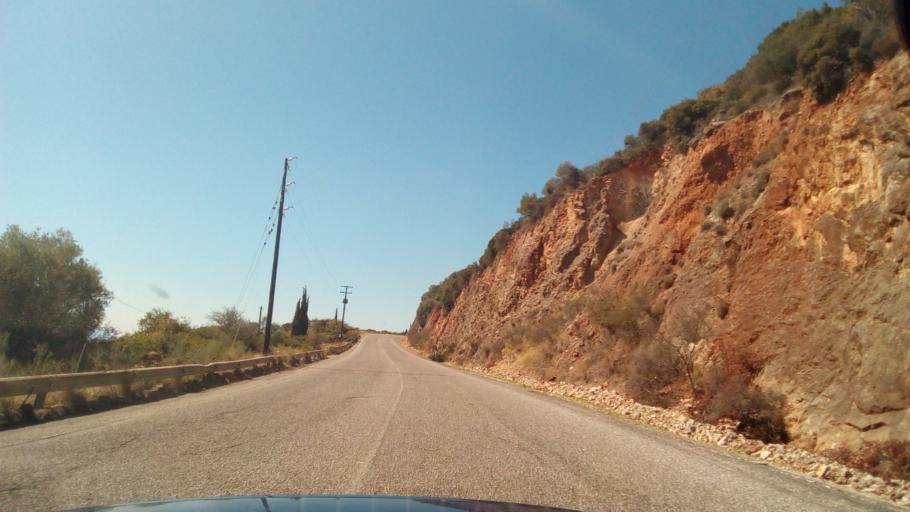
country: GR
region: West Greece
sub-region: Nomos Achaias
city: Kamarai
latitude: 38.3954
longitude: 22.0510
